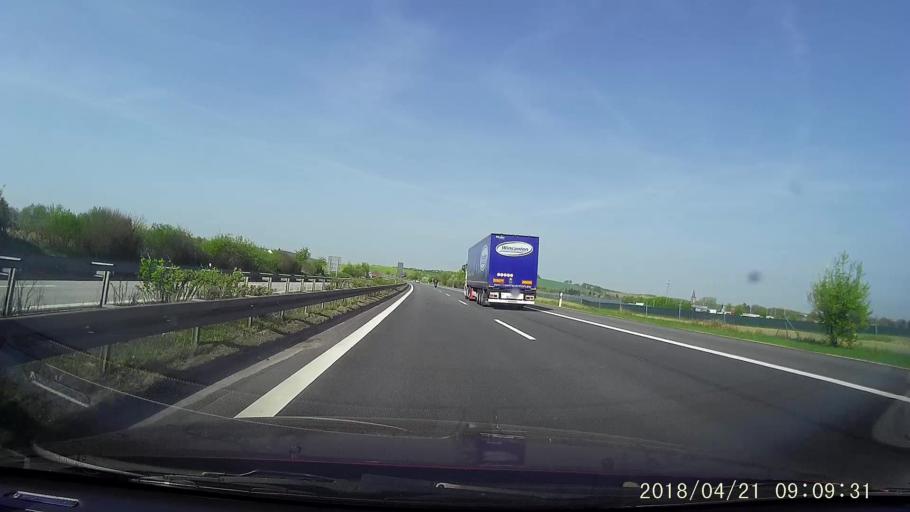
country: DE
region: Saxony
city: Kodersdorf
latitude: 51.2233
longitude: 14.9077
